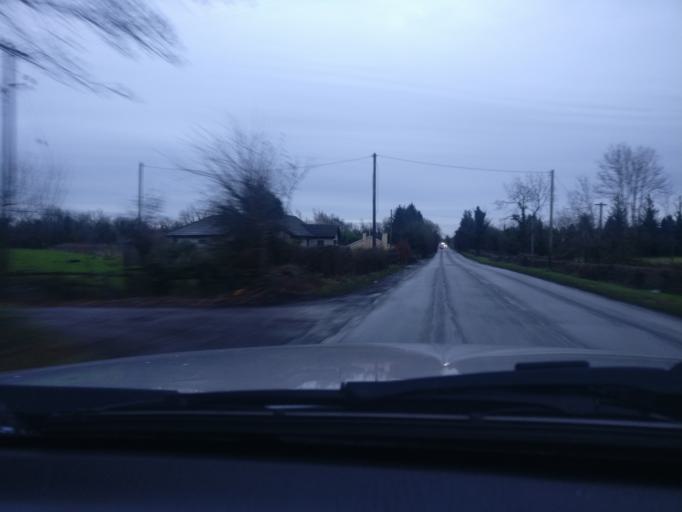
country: IE
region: Leinster
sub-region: An Mhi
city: Navan
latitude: 53.6790
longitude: -6.7531
